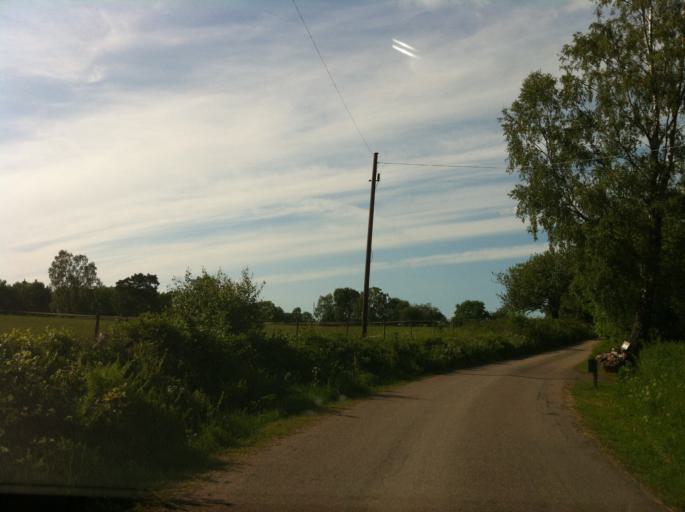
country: SE
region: Skane
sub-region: Klippans Kommun
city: Ljungbyhed
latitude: 56.0503
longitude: 13.2215
